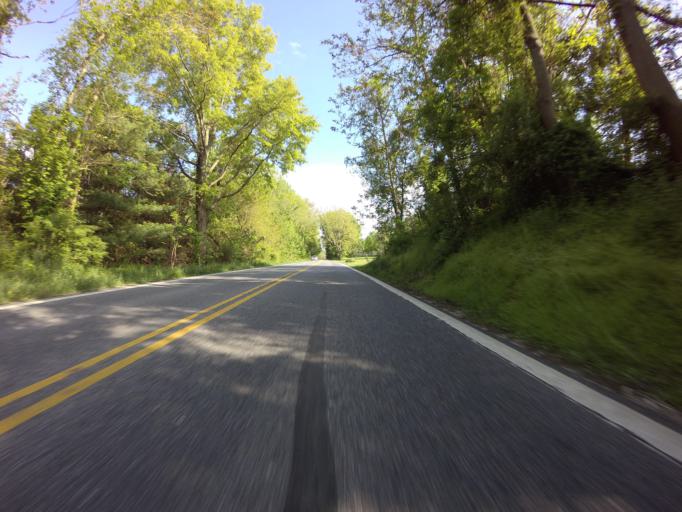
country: US
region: Maryland
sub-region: Baltimore County
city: Hunt Valley
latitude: 39.5136
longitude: -76.7161
